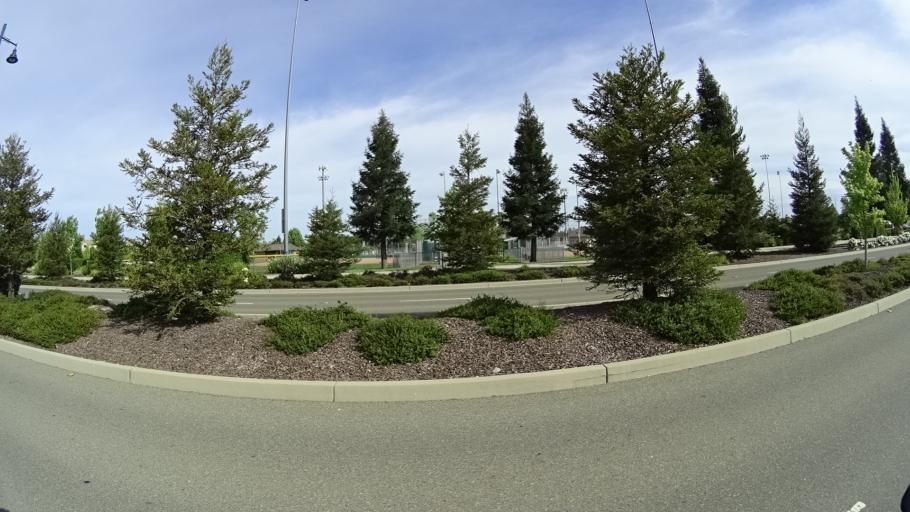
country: US
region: California
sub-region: Placer County
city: Lincoln
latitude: 38.8308
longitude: -121.2864
